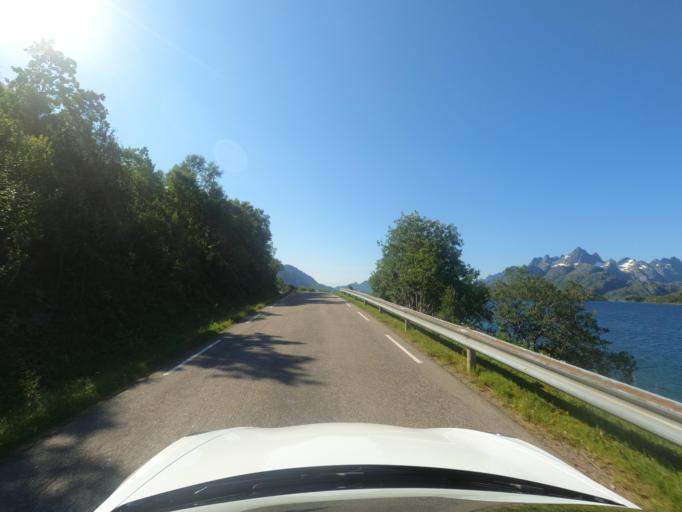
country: NO
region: Nordland
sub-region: Hadsel
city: Stokmarknes
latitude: 68.3743
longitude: 15.0775
